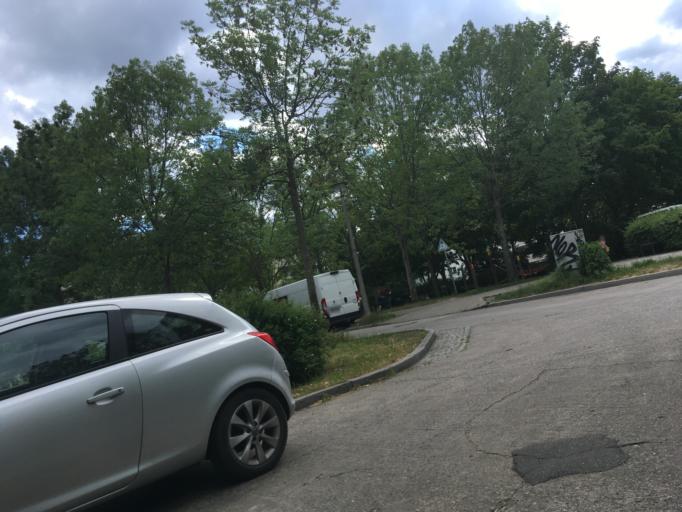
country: DE
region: Berlin
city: Falkenberg
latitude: 52.5673
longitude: 13.5304
